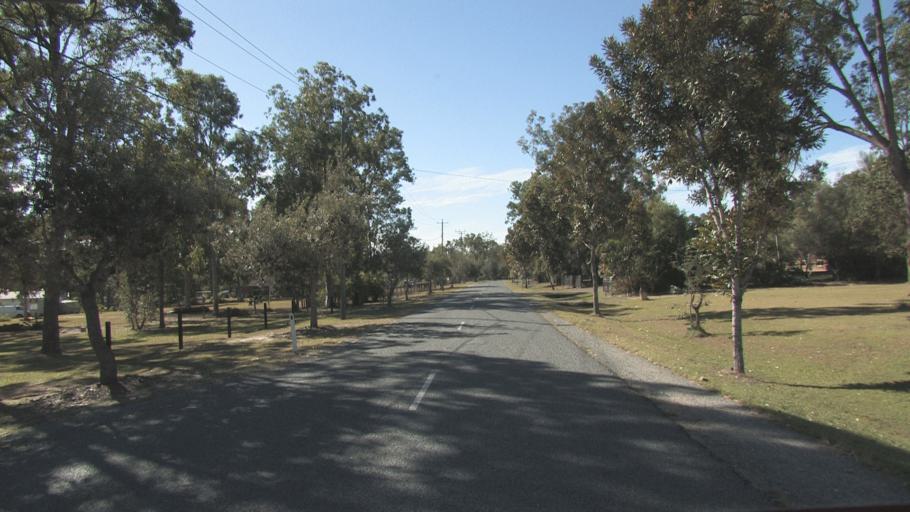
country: AU
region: Queensland
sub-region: Logan
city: North Maclean
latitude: -27.7437
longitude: 152.9549
